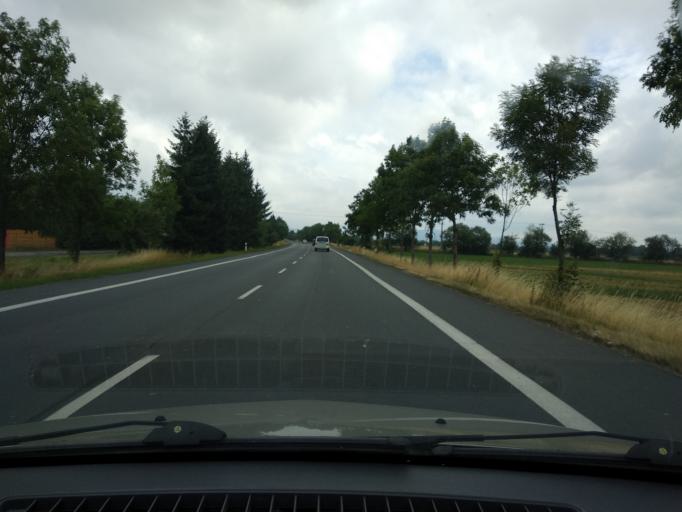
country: CZ
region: Olomoucky
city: Zabreh
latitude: 49.8801
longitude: 16.8932
